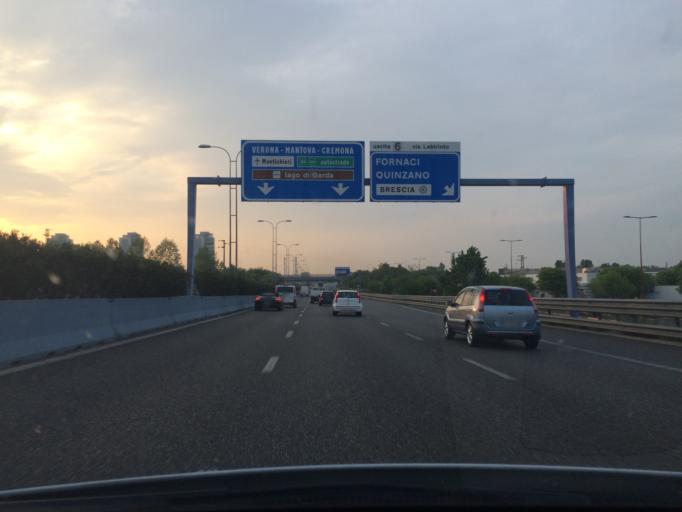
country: IT
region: Lombardy
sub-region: Provincia di Brescia
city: Brescia
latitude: 45.5221
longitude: 10.1857
